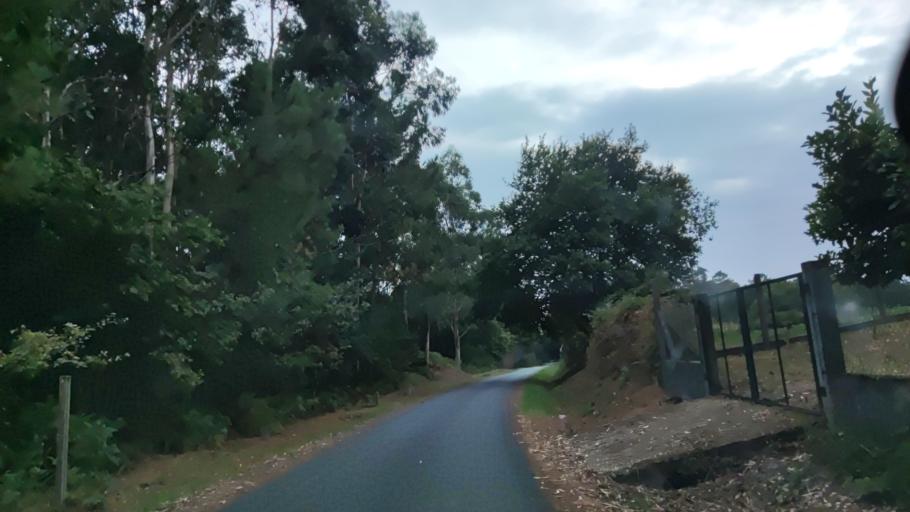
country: ES
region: Galicia
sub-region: Provincia da Coruna
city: Padron
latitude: 42.7158
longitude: -8.6858
